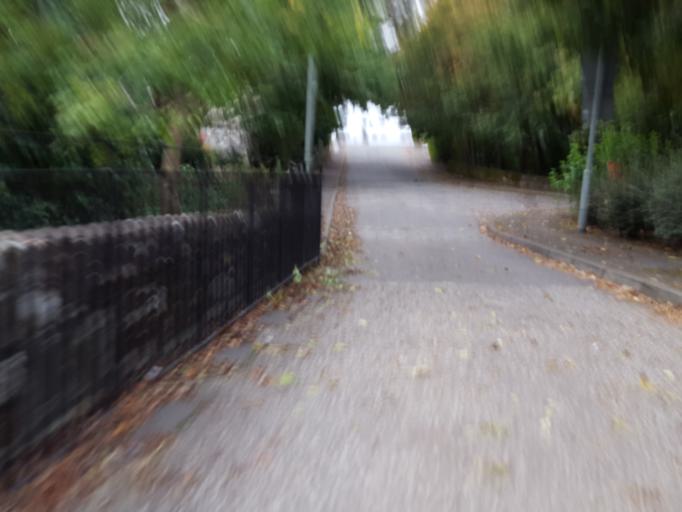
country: GB
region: Scotland
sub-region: West Lothian
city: Livingston
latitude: 55.8846
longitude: -3.5390
